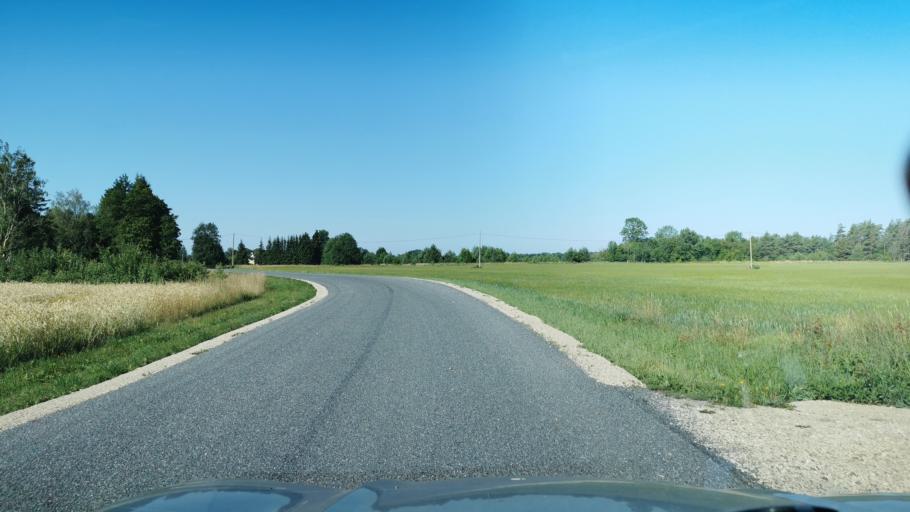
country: EE
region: Harju
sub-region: Paldiski linn
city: Paldiski
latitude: 59.2121
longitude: 24.0246
